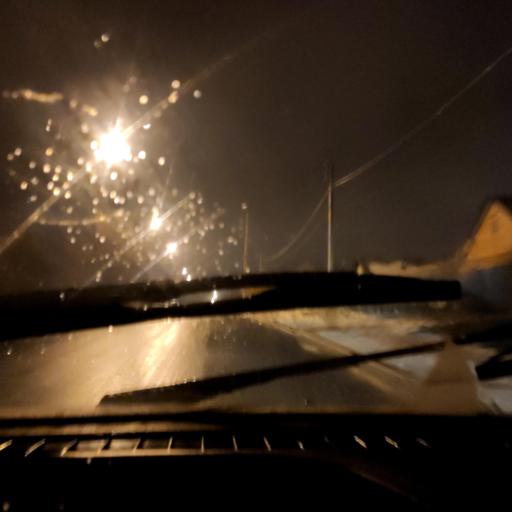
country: RU
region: Samara
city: Zhigulevsk
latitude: 53.4855
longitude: 49.5272
